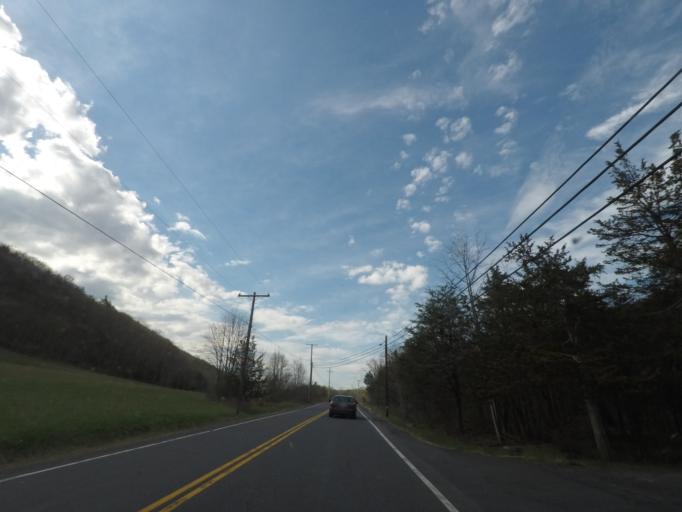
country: US
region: New York
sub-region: Albany County
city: Voorheesville
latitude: 42.5642
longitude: -73.9527
